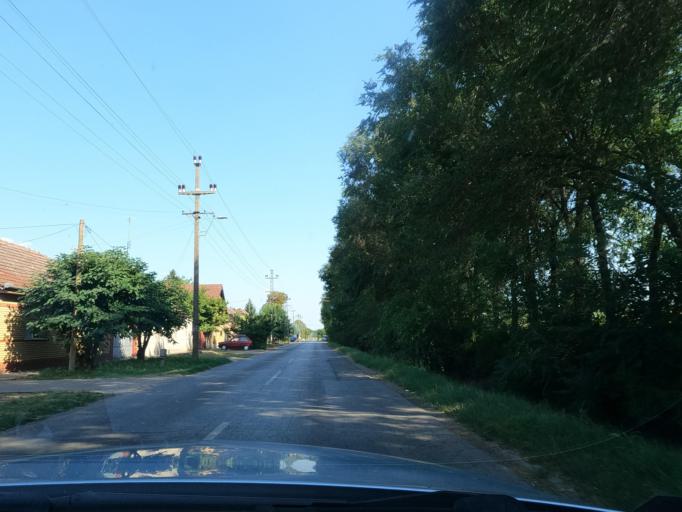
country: RS
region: Autonomna Pokrajina Vojvodina
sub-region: Juznobacki Okrug
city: Becej
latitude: 45.6284
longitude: 20.0222
